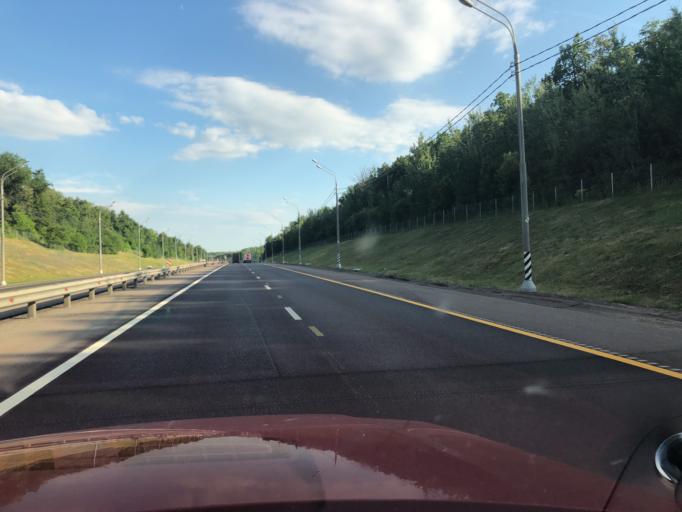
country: RU
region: Lipetsk
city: Zadonsk
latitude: 52.3994
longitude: 38.8596
